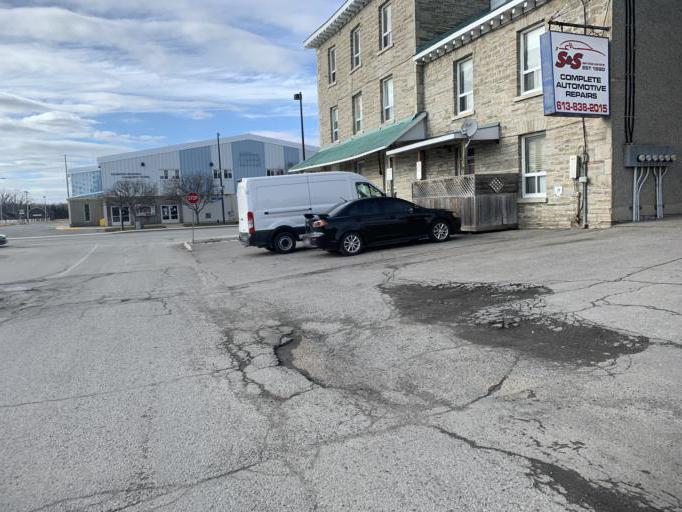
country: CA
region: Ontario
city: Bells Corners
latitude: 45.1949
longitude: -75.8371
